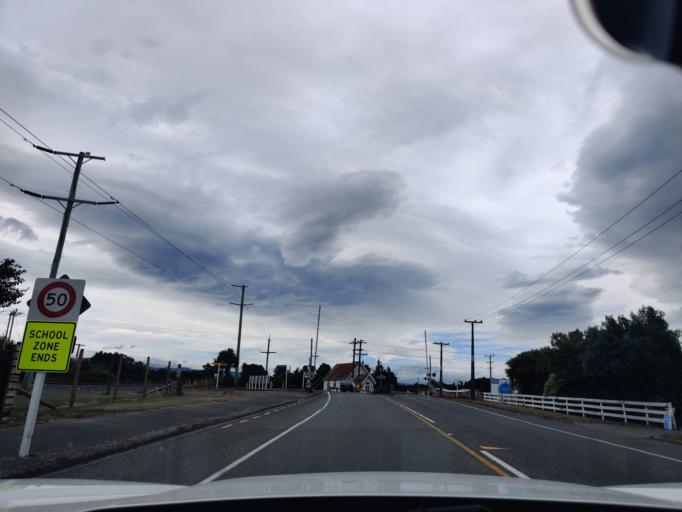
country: NZ
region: Wellington
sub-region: Masterton District
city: Masterton
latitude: -40.9588
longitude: 175.6139
